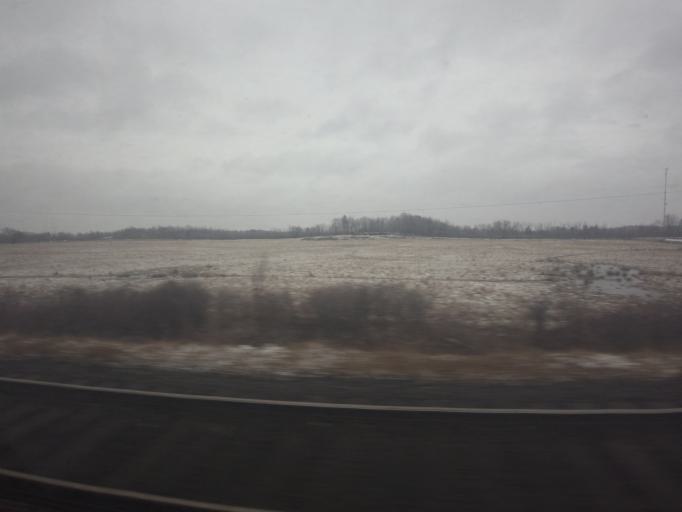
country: CA
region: Ontario
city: Gananoque
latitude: 44.3274
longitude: -76.3251
